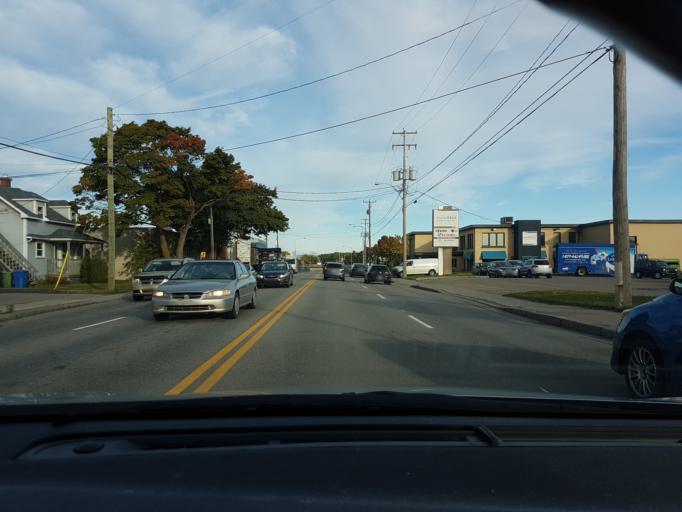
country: CA
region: Quebec
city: Quebec
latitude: 46.8019
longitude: -71.2615
